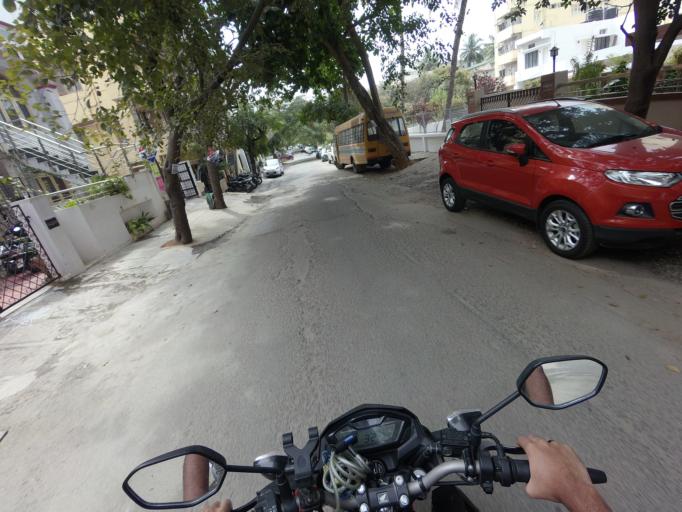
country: IN
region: Karnataka
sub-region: Bangalore Urban
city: Bangalore
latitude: 12.9617
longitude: 77.5345
